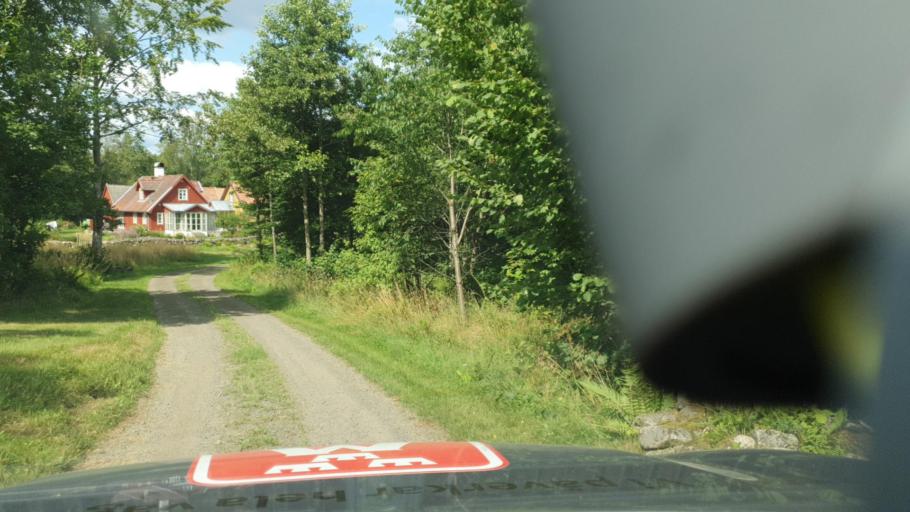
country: SE
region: Skane
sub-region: Hassleholms Kommun
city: Vinslov
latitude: 56.0441
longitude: 13.8677
